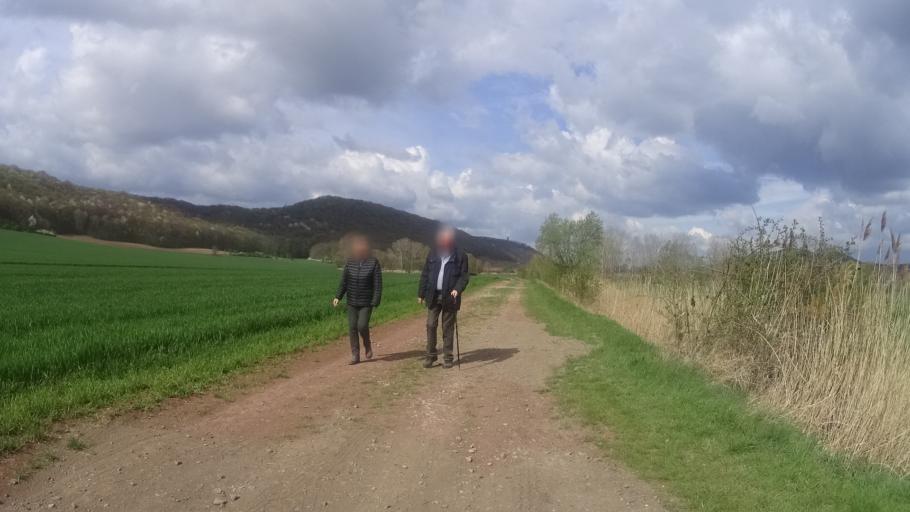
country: DE
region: Thuringia
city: Wandersleben
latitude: 50.8644
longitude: 10.8606
